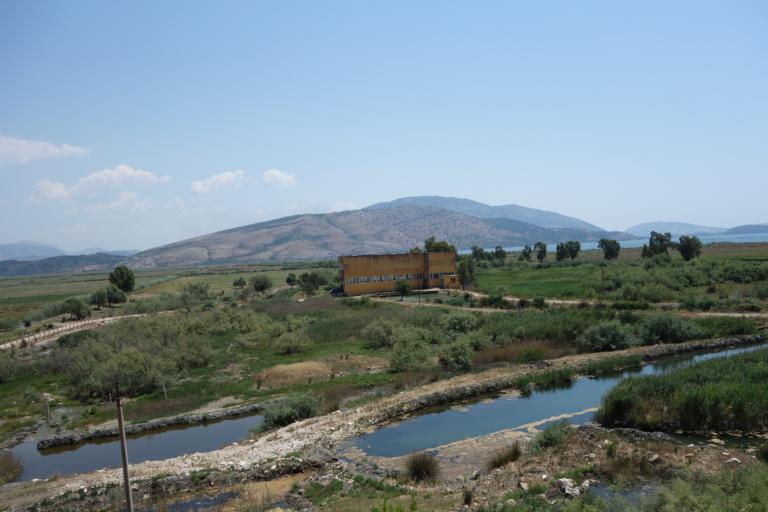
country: AL
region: Vlore
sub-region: Rrethi i Sarandes
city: Sarande
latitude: 39.8203
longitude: 20.0187
